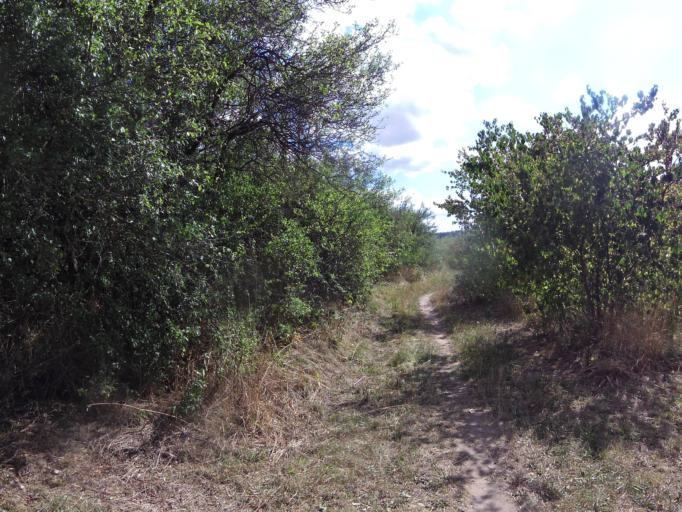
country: DE
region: Bavaria
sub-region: Regierungsbezirk Unterfranken
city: Eibelstadt
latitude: 49.7340
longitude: 9.9952
